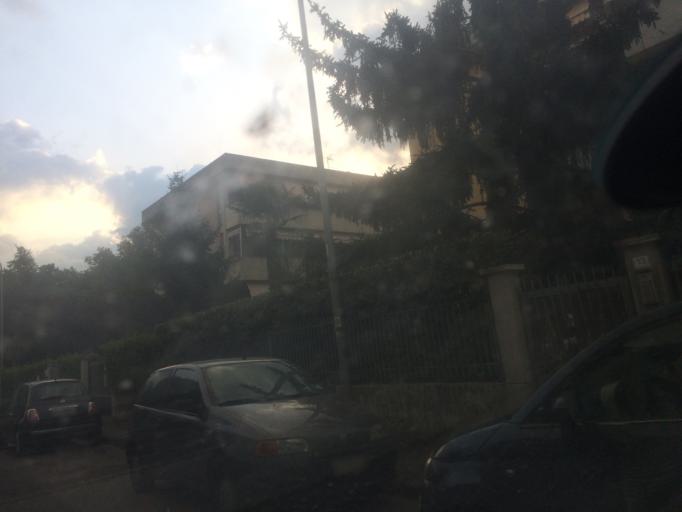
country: IT
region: Tuscany
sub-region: Provincia di Massa-Carrara
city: Massa
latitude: 44.0208
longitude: 10.0916
